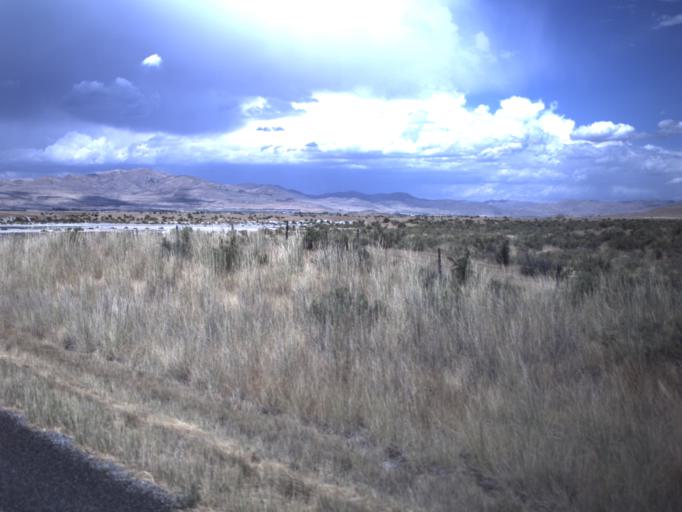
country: US
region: Utah
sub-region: Box Elder County
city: Tremonton
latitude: 41.5854
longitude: -112.2638
